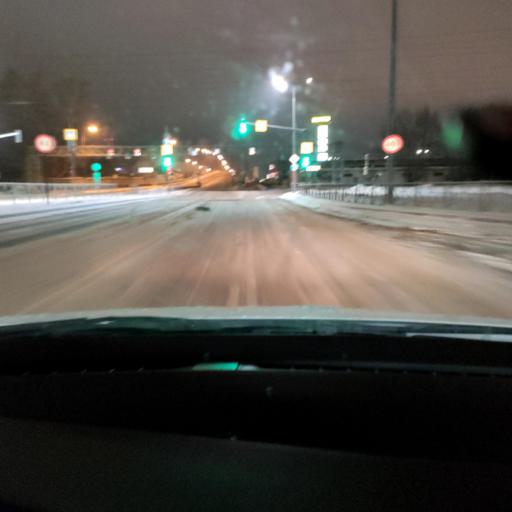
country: RU
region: Tatarstan
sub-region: Gorod Kazan'
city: Kazan
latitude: 55.7307
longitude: 49.1355
